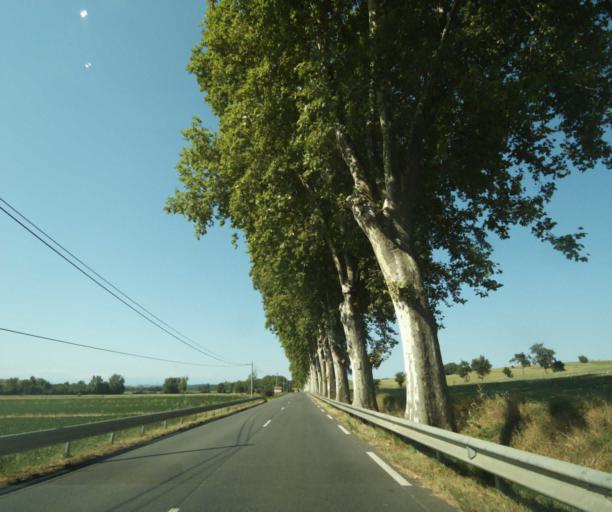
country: FR
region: Midi-Pyrenees
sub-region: Departement de la Haute-Garonne
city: Beaumont-sur-Leze
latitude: 43.3799
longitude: 1.3421
